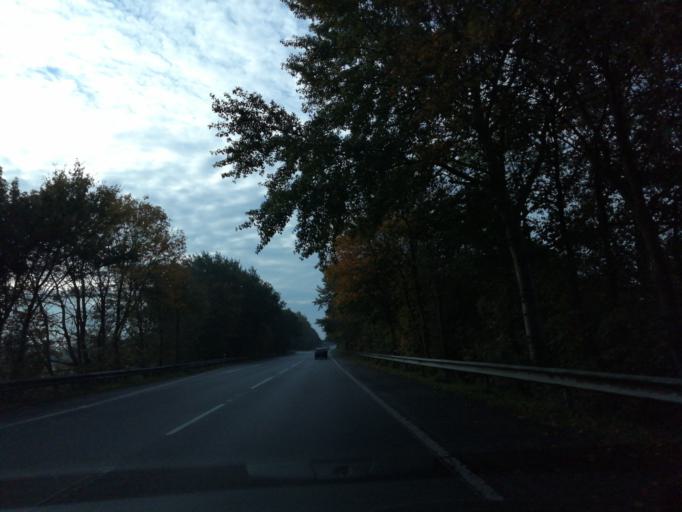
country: DE
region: Lower Saxony
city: Fedderwarden
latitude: 53.5823
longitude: 8.0566
